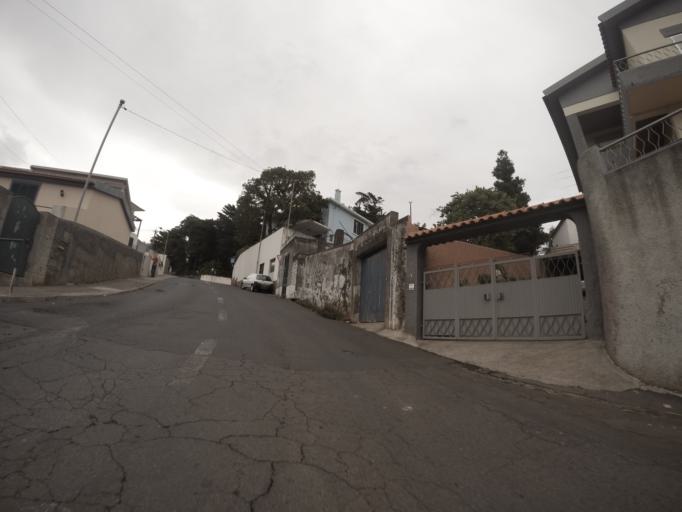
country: PT
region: Madeira
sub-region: Funchal
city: Nossa Senhora do Monte
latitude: 32.6598
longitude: -16.9230
